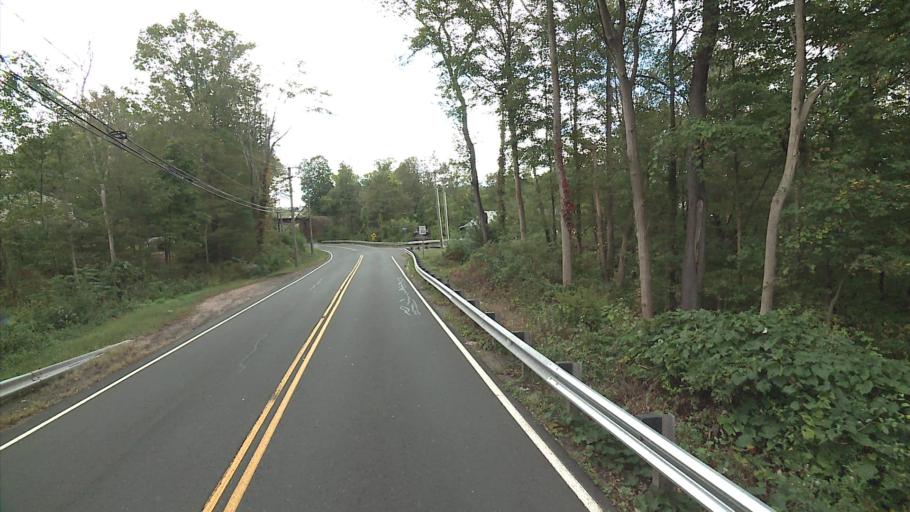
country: US
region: Connecticut
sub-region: Middlesex County
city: Durham
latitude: 41.4754
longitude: -72.7274
